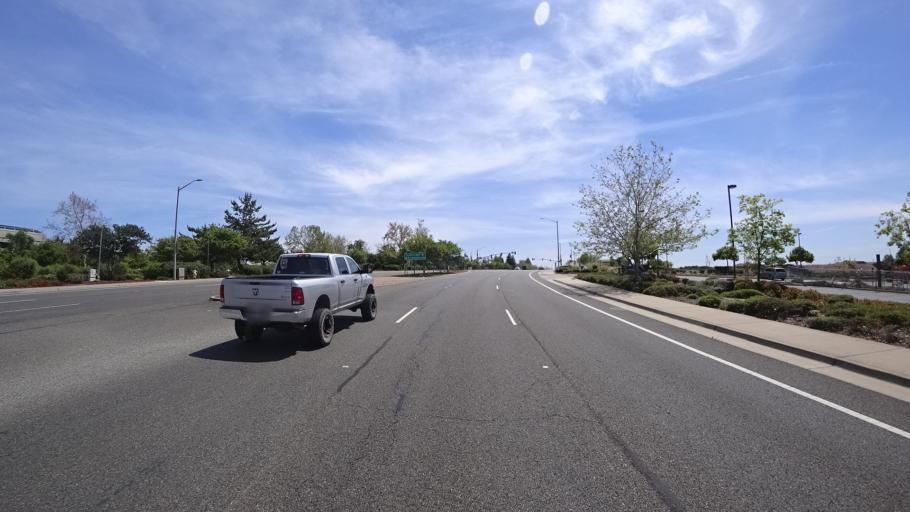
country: US
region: California
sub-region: Placer County
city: Rocklin
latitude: 38.8165
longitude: -121.2880
